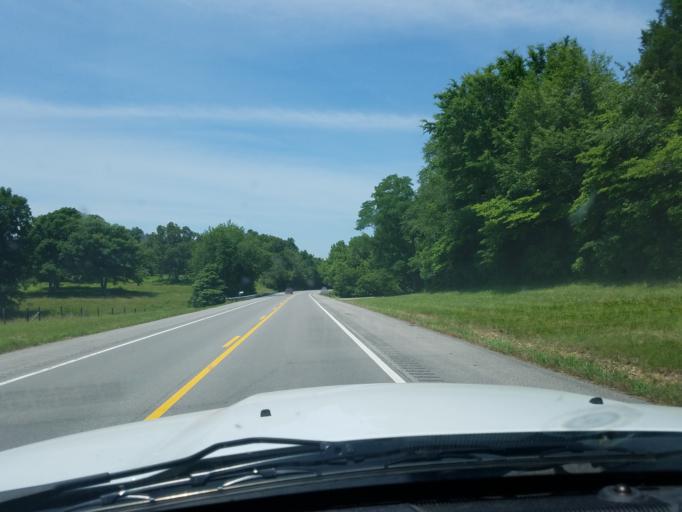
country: US
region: Tennessee
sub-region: Sumner County
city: Westmoreland
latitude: 36.5841
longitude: -86.2389
